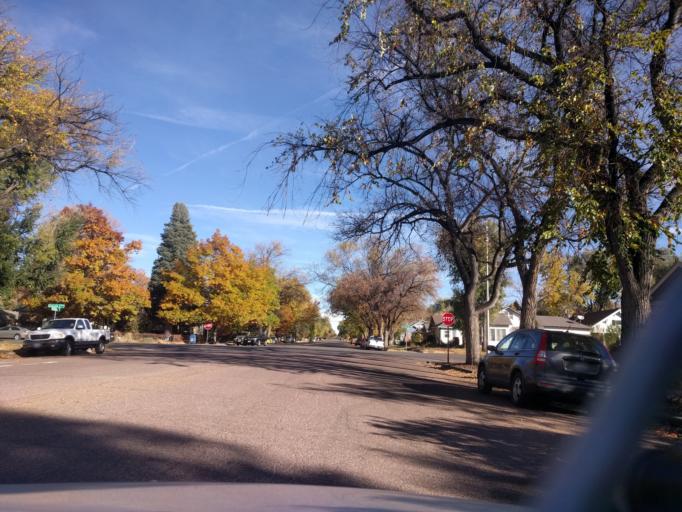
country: US
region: Colorado
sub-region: El Paso County
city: Colorado Springs
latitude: 38.8499
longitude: -104.8155
